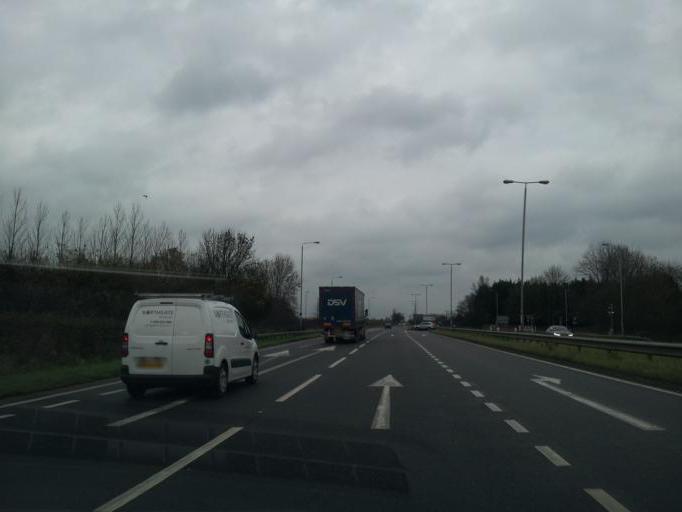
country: GB
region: England
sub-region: Leicestershire
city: Queniborough
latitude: 52.7417
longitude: -1.0655
